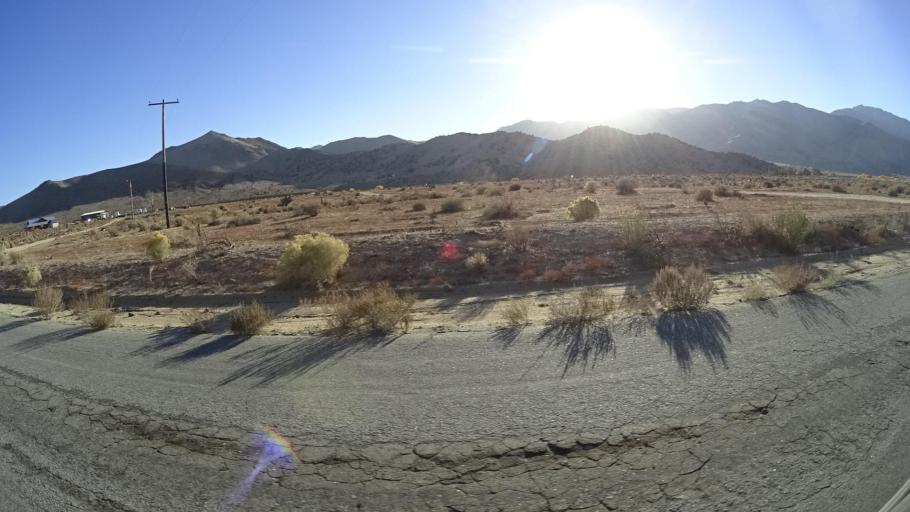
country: US
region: California
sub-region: Kern County
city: Weldon
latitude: 35.5572
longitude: -118.2276
